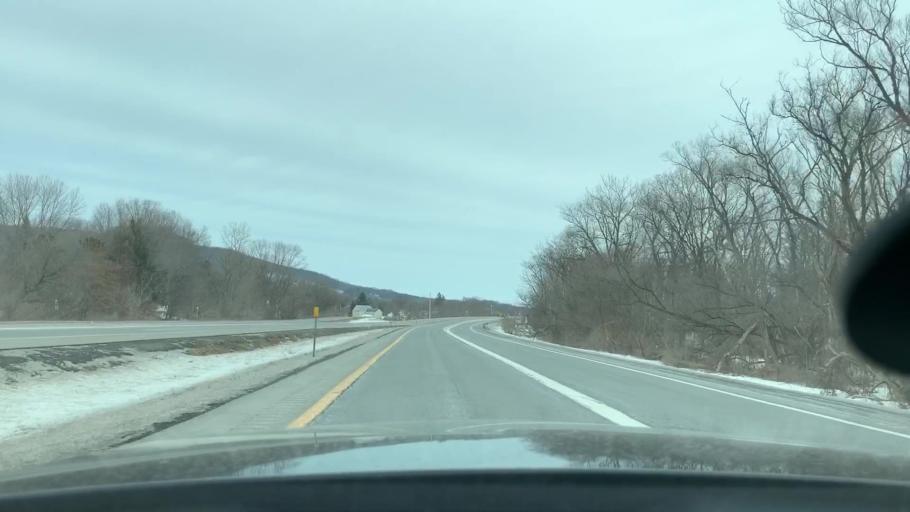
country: US
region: New York
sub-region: Herkimer County
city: Frankfort
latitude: 43.0247
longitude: -75.0621
